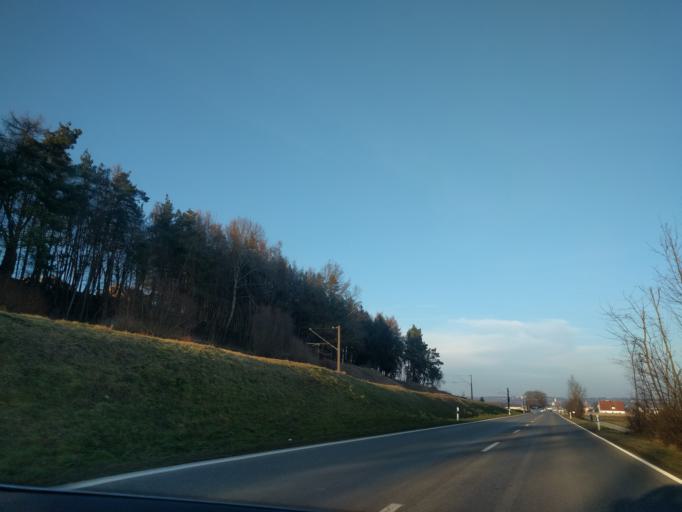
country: DE
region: Bavaria
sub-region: Swabia
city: Donauwoerth
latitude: 48.6977
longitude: 10.7402
